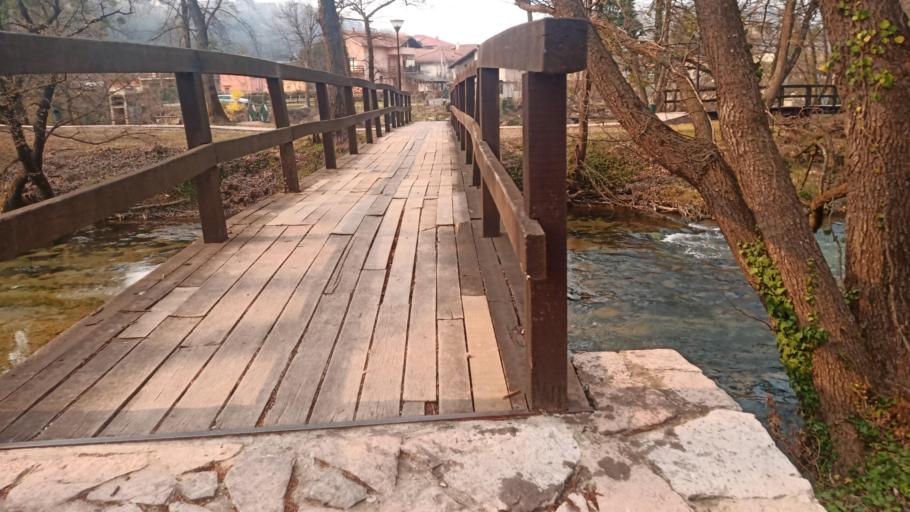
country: BA
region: Federation of Bosnia and Herzegovina
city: Bosanska Krupa
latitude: 44.8881
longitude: 16.1573
